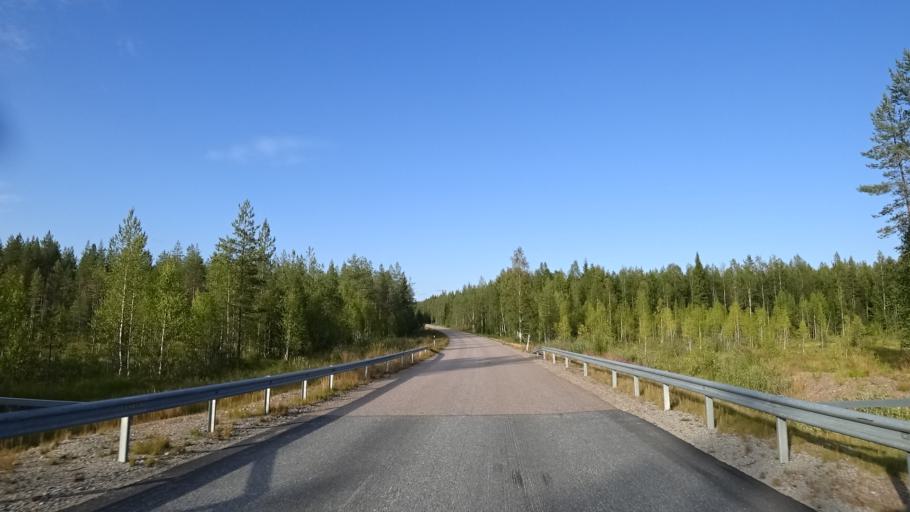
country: FI
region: North Karelia
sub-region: Joensuu
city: Eno
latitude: 63.0293
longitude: 30.5225
